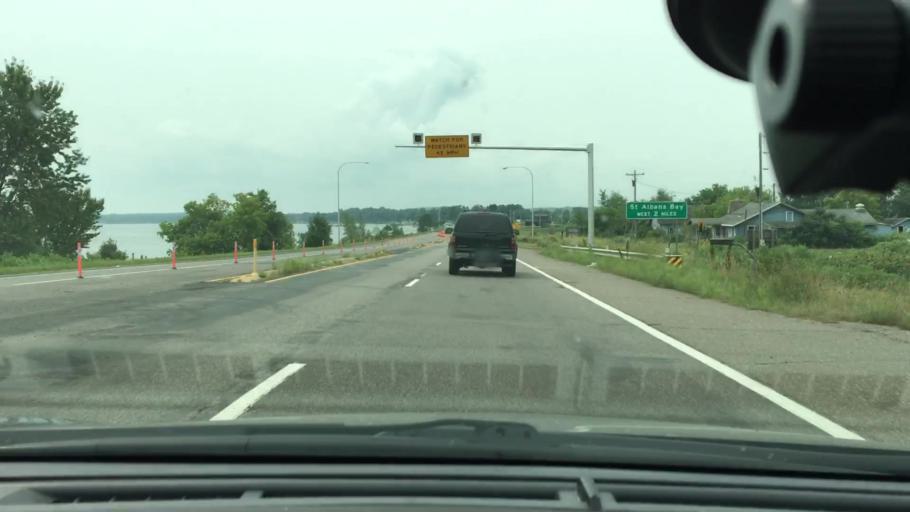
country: US
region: Minnesota
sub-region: Mille Lacs County
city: Vineland
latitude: 46.2781
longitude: -93.8204
